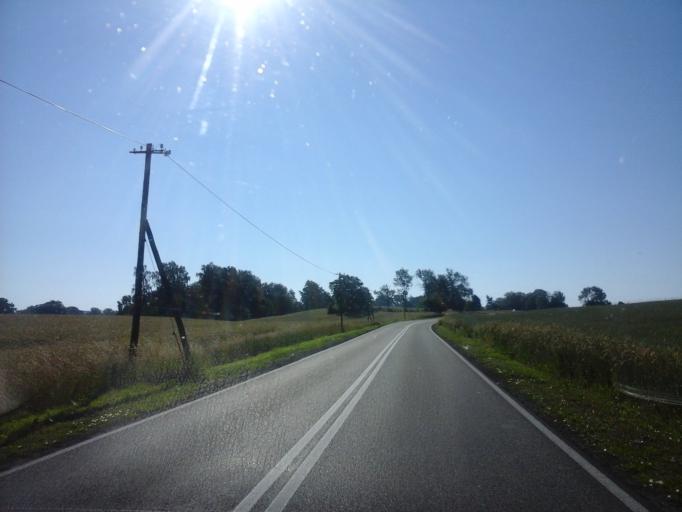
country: PL
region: West Pomeranian Voivodeship
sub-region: Powiat lobeski
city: Wegorzyno
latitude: 53.5059
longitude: 15.6541
